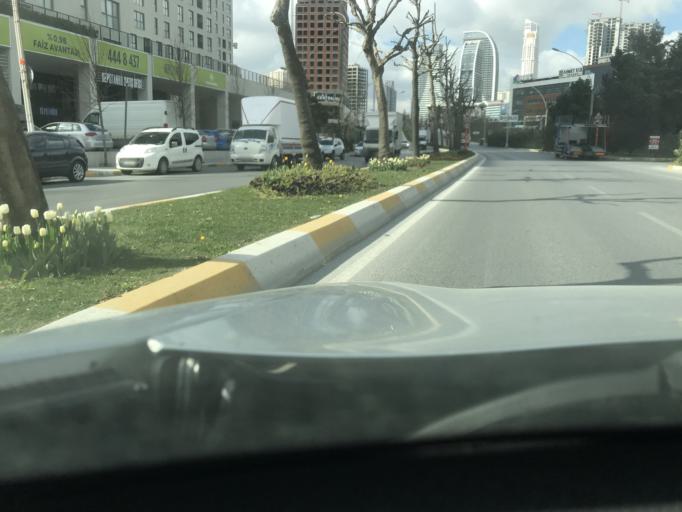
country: TR
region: Istanbul
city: Esenyurt
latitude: 41.0083
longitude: 28.6820
